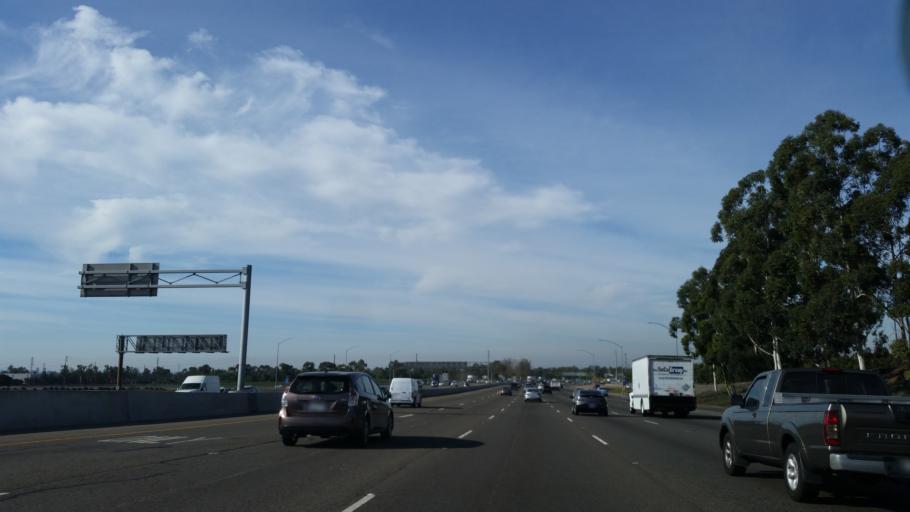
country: US
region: California
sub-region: Orange County
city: Irvine
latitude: 33.6794
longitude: -117.7598
